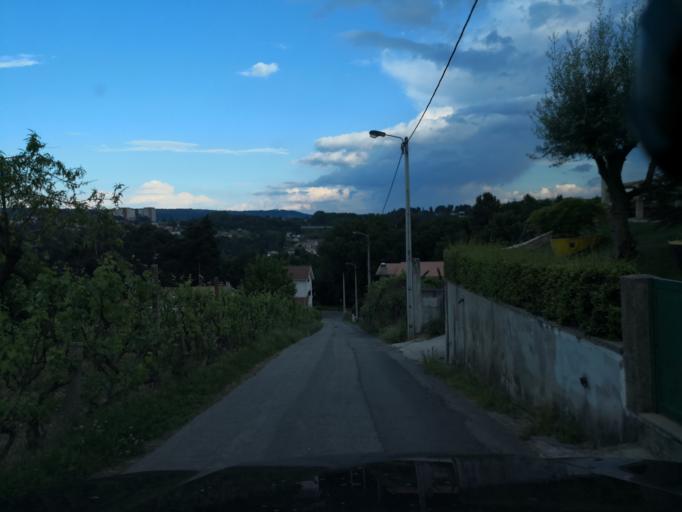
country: PT
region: Vila Real
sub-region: Vila Real
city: Vila Real
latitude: 41.3197
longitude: -7.7475
